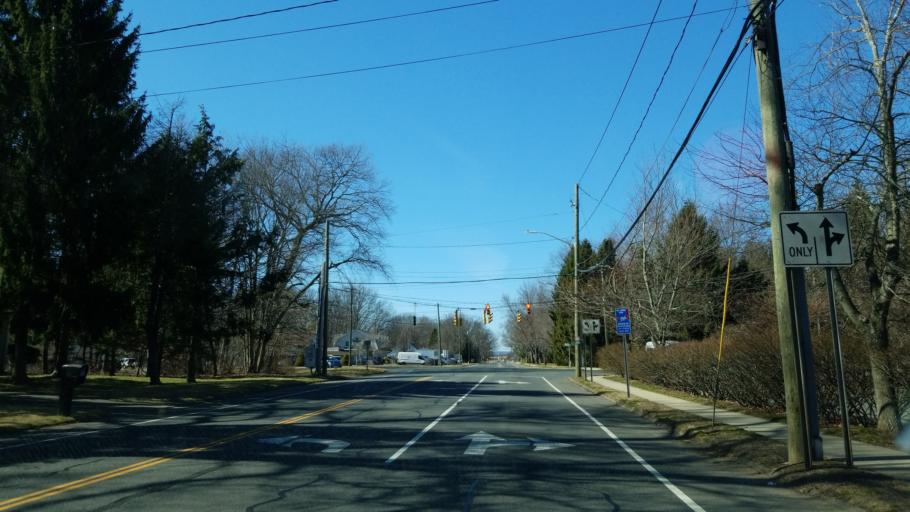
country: US
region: Connecticut
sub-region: Hartford County
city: South Windsor
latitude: 41.8086
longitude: -72.6012
